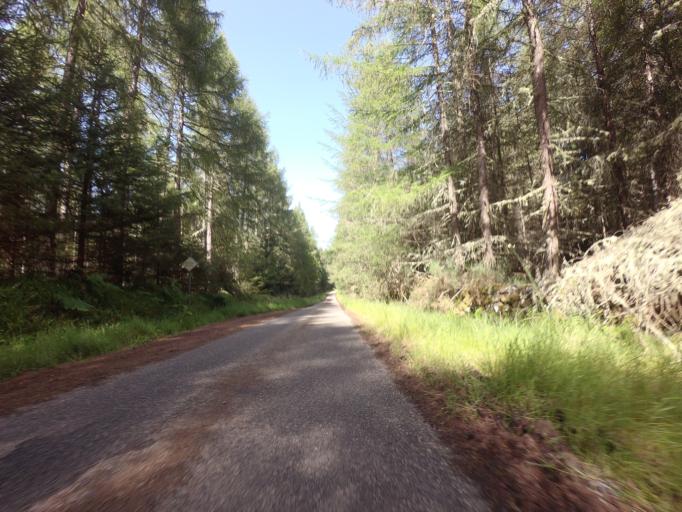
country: GB
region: Scotland
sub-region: Highland
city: Nairn
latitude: 57.5021
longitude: -3.9308
